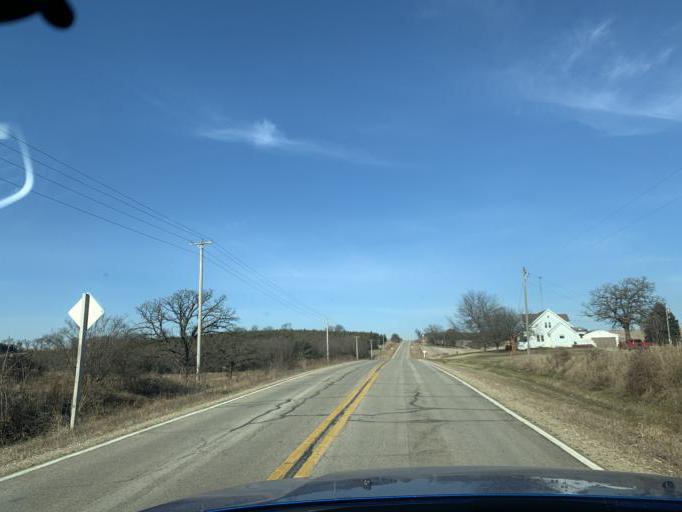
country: US
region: Wisconsin
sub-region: Green County
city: New Glarus
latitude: 42.7657
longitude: -89.8582
